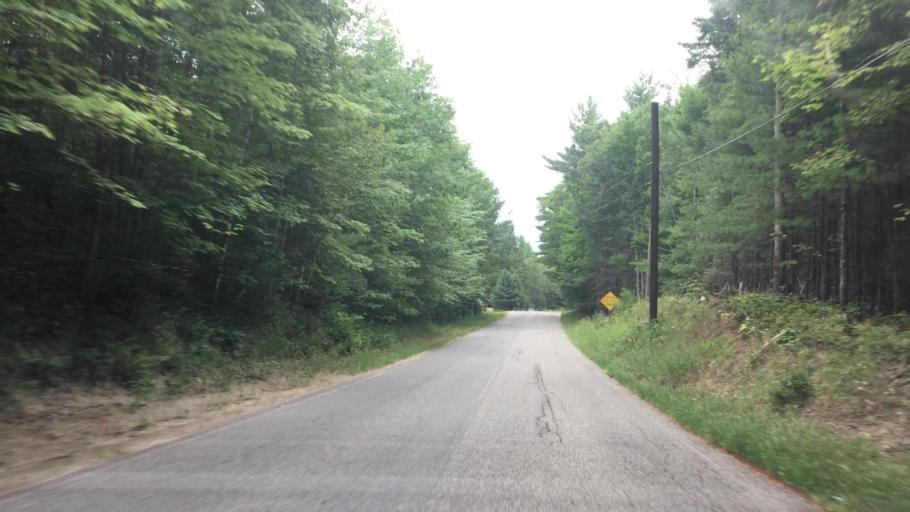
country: US
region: New York
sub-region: Essex County
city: Keeseville
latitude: 44.4118
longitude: -73.6510
